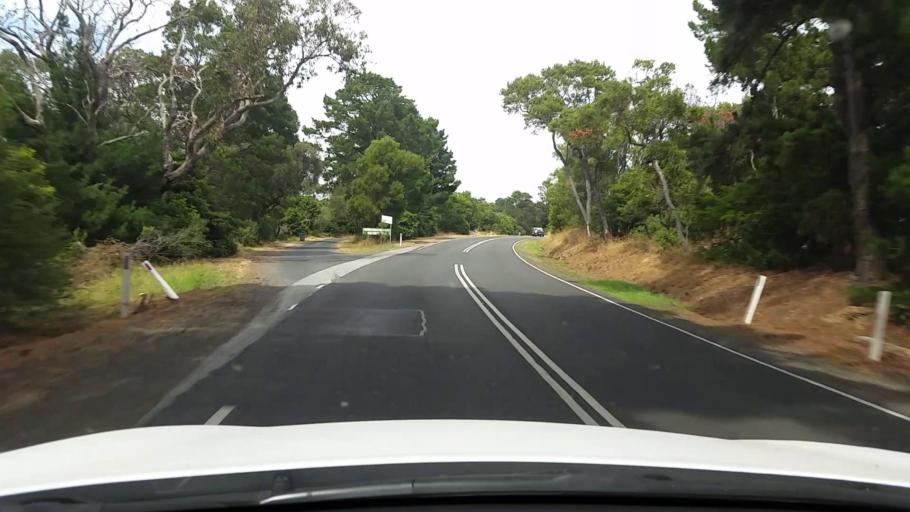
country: AU
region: Victoria
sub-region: Mornington Peninsula
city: Merricks
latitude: -38.3814
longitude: 145.1098
